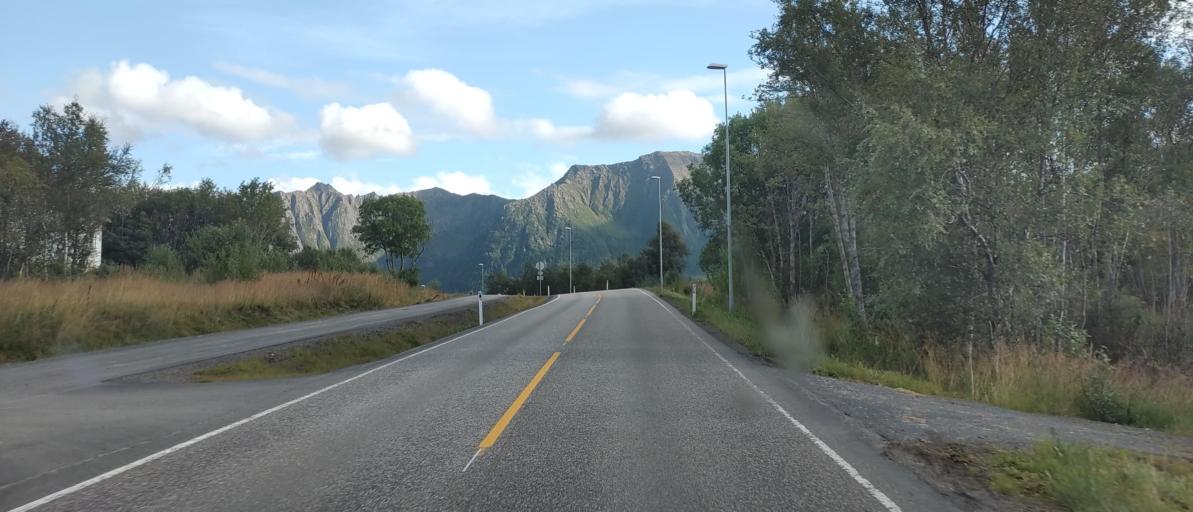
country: NO
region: Nordland
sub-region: Sortland
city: Sortland
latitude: 68.7447
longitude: 15.5069
